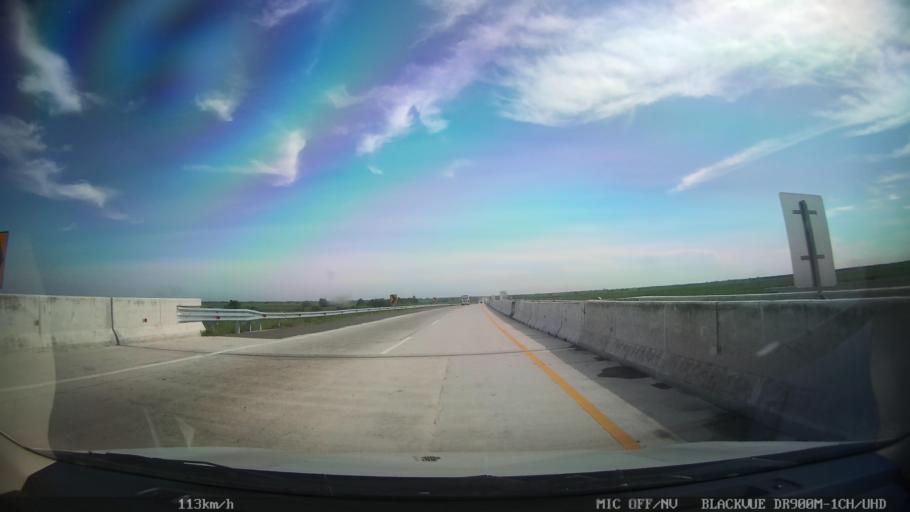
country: ID
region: North Sumatra
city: Binjai
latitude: 3.6628
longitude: 98.5325
